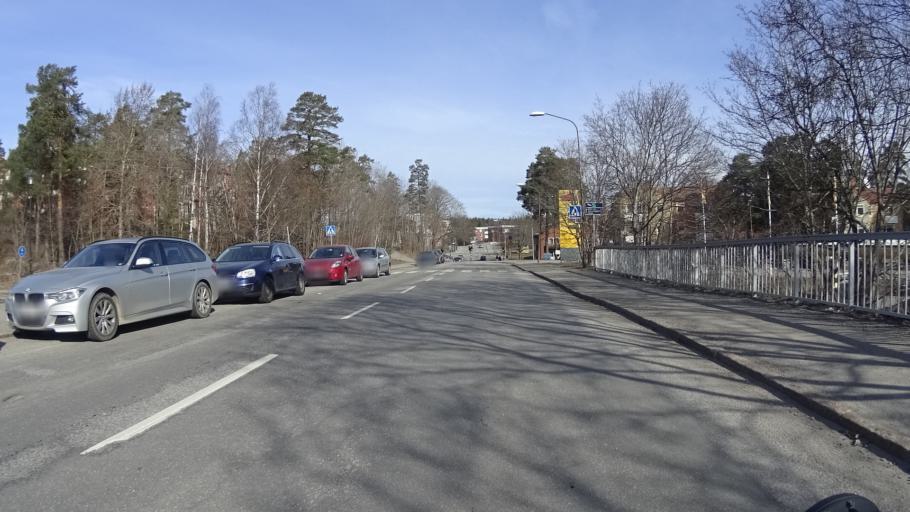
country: SE
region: Stockholm
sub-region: Nacka Kommun
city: Nacka
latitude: 59.2780
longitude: 18.1272
